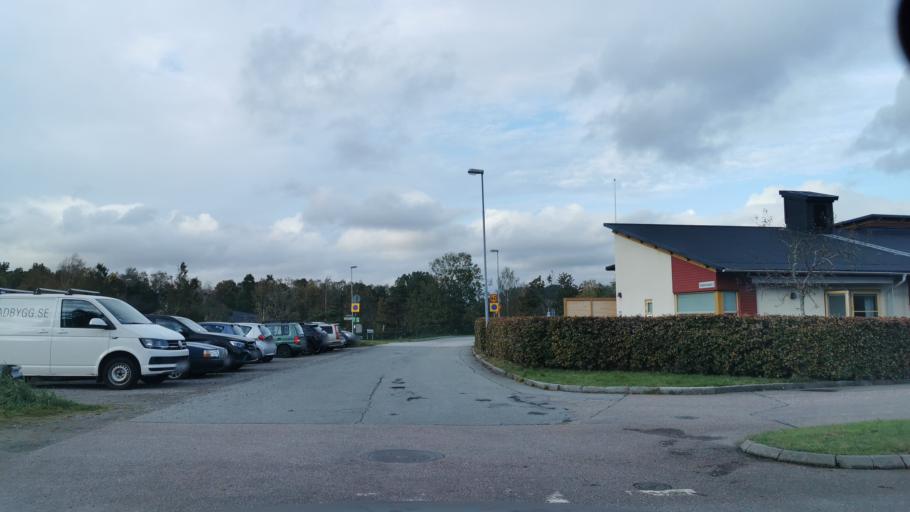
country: SE
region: Vaestra Goetaland
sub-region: Partille Kommun
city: Partille
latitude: 57.7150
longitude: 12.0745
